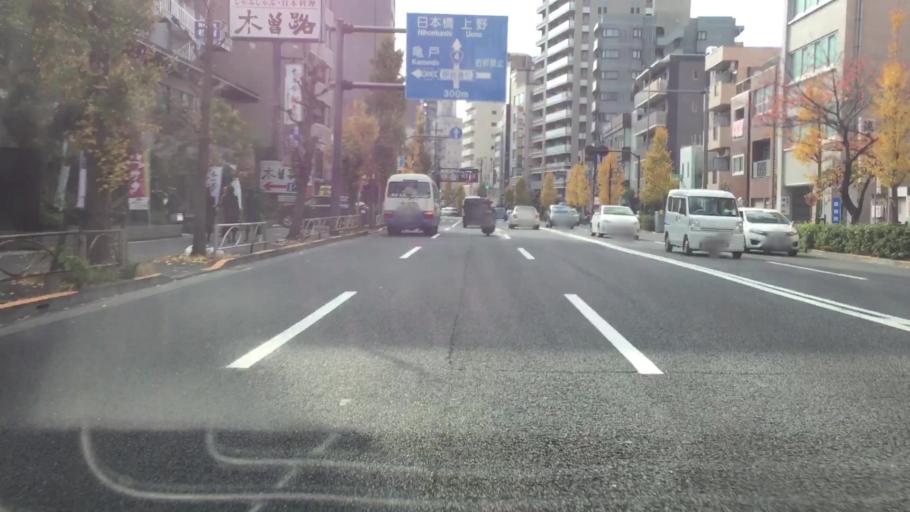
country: JP
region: Saitama
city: Soka
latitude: 35.7335
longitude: 139.7936
